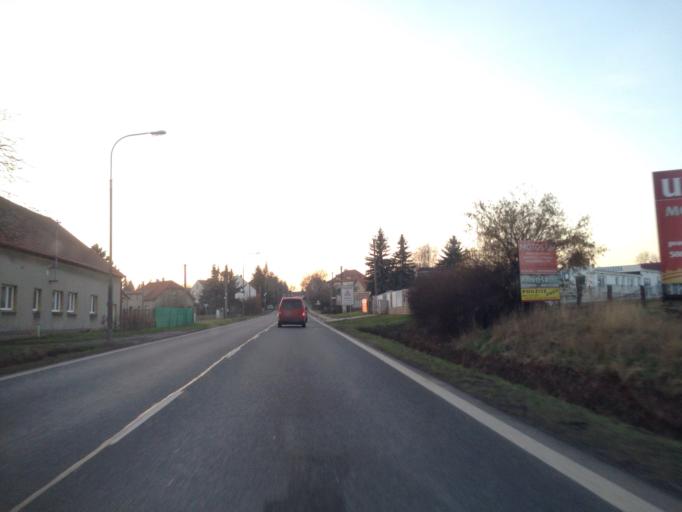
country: CZ
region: Central Bohemia
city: Revnicov
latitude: 50.1802
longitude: 13.8142
